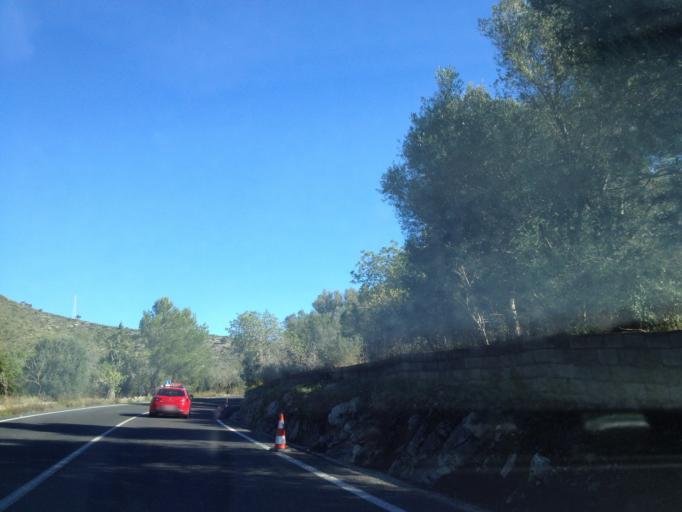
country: ES
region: Balearic Islands
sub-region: Illes Balears
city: Sant Llorenc des Cardassar
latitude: 39.6384
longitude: 3.3065
